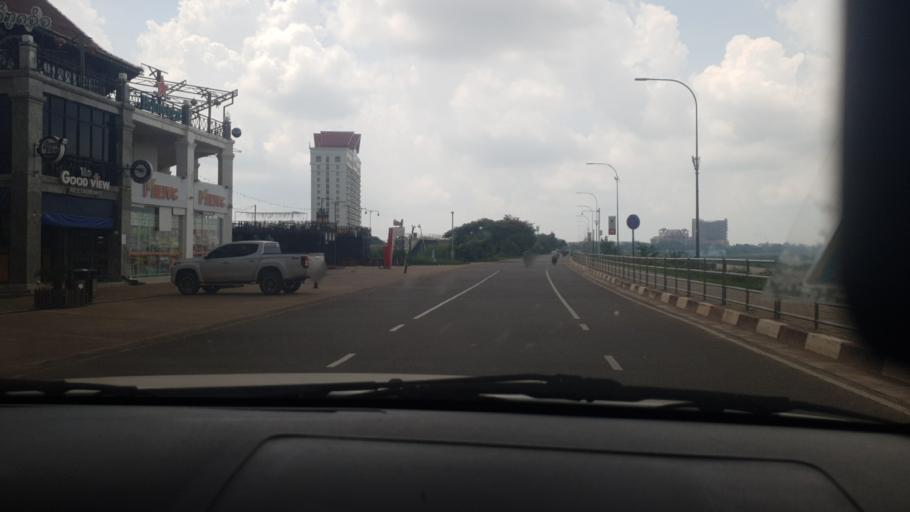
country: LA
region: Vientiane
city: Vientiane
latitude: 17.9579
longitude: 102.6108
